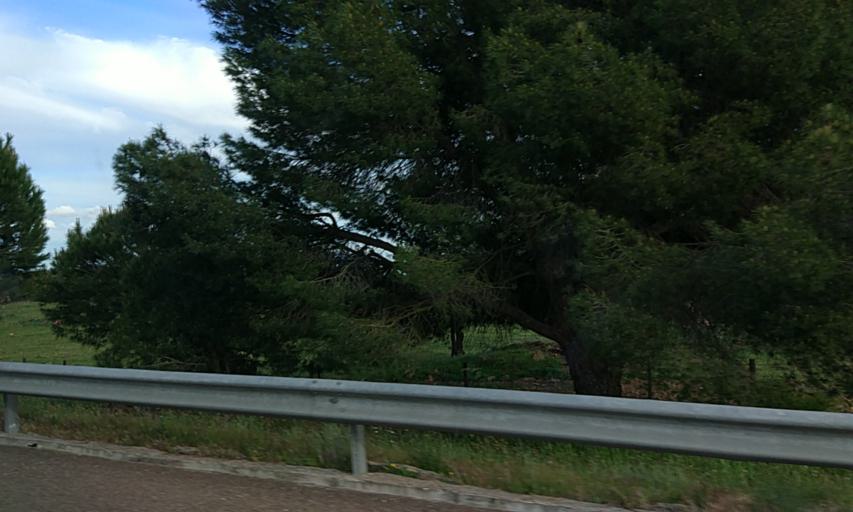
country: PT
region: Portalegre
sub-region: Elvas
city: Elvas
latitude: 38.8997
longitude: -7.2008
